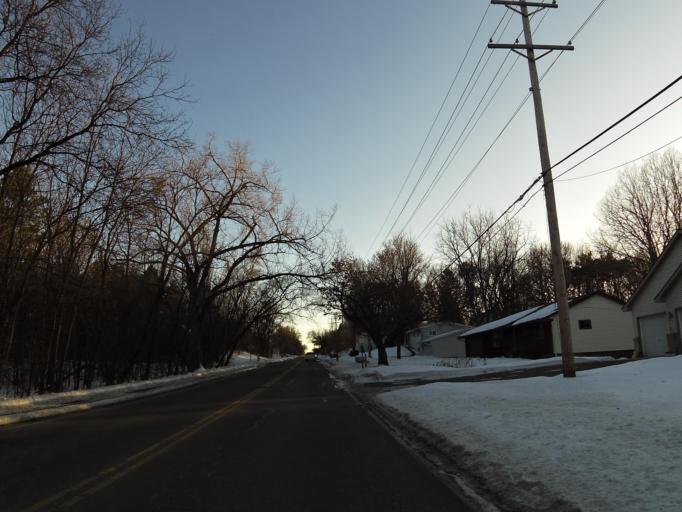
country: US
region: Minnesota
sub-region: Ramsey County
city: North Saint Paul
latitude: 45.0259
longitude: -93.0356
